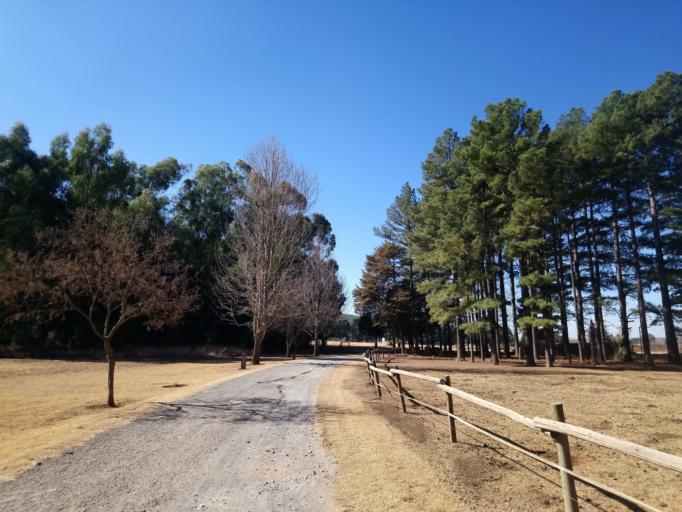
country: ZA
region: KwaZulu-Natal
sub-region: uMgungundlovu District Municipality
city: Mooirivier
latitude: -29.3230
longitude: 29.7167
